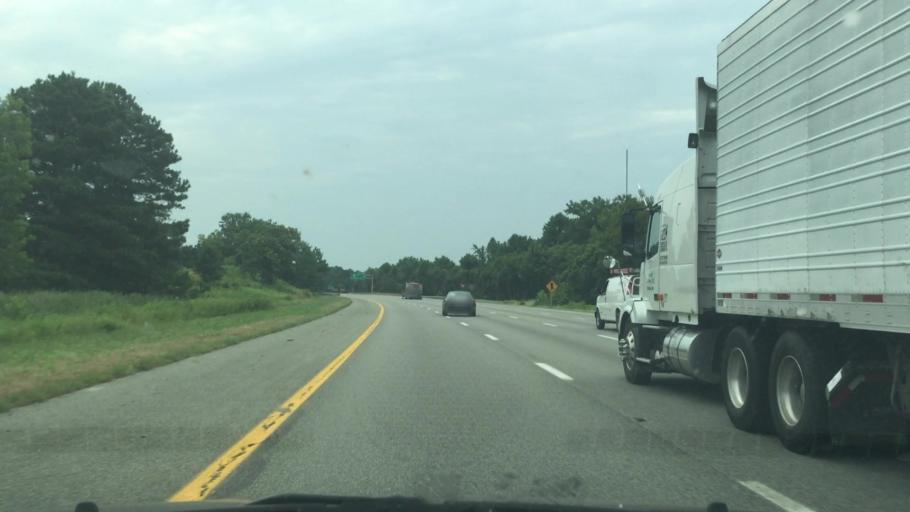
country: US
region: Virginia
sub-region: Henrico County
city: Highland Springs
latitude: 37.5822
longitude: -77.3326
